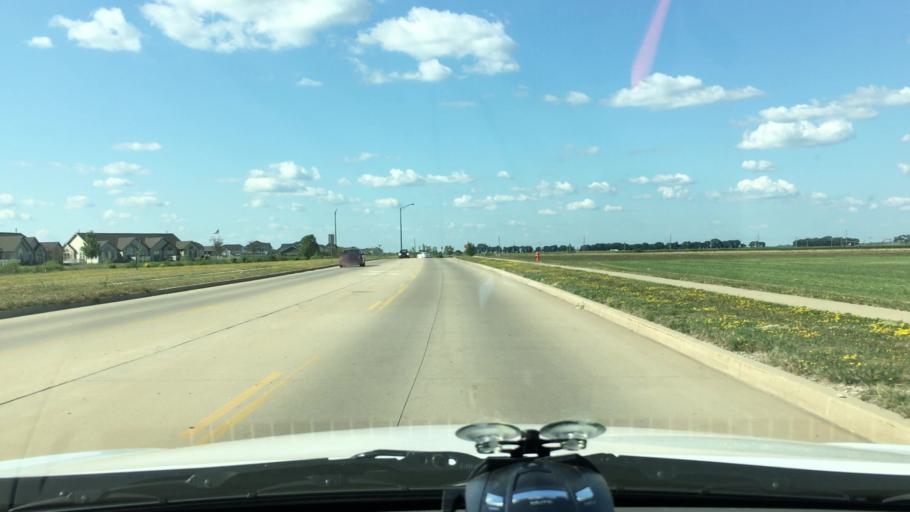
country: US
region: Illinois
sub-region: Champaign County
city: Champaign
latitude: 40.1470
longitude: -88.2484
